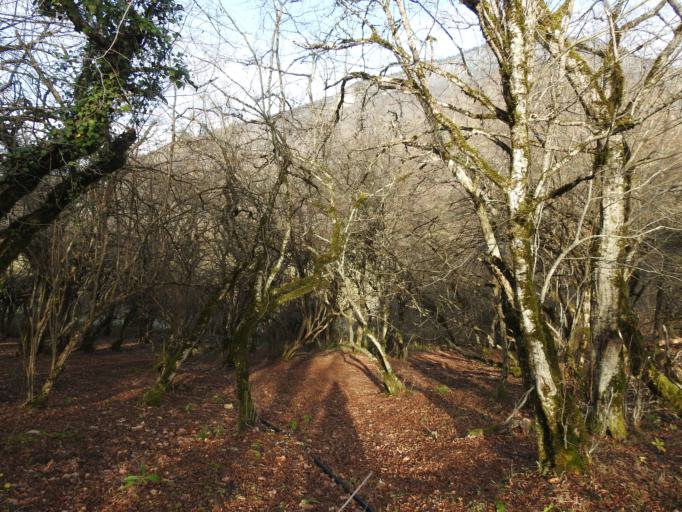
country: GE
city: Gantiadi
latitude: 43.4161
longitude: 40.2149
